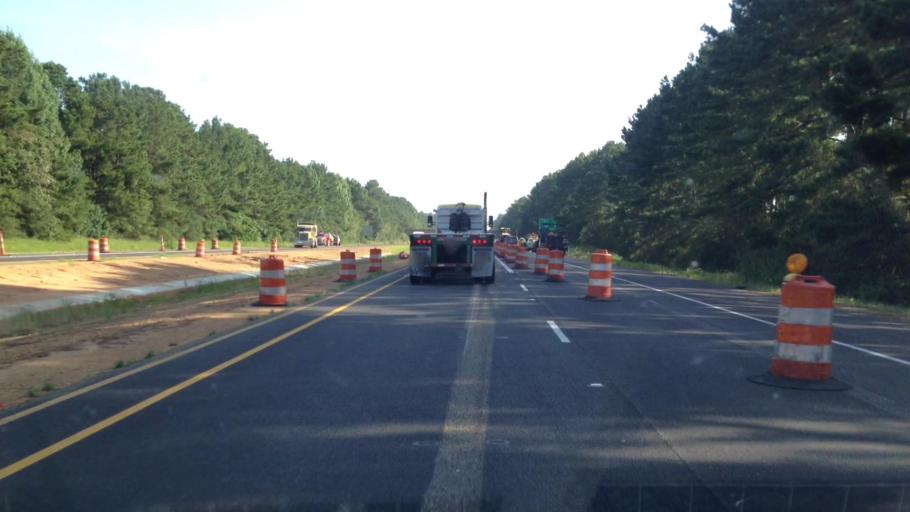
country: US
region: Mississippi
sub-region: Pike County
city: McComb
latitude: 31.2006
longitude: -90.4840
